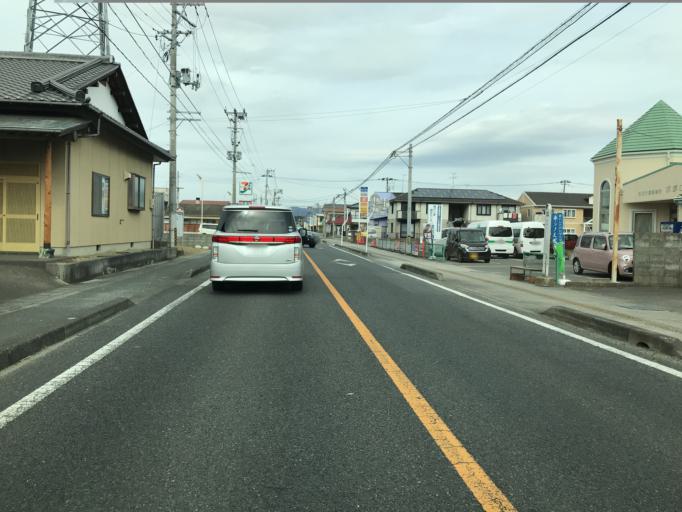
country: JP
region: Fukushima
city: Iwaki
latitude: 37.0755
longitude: 140.8815
